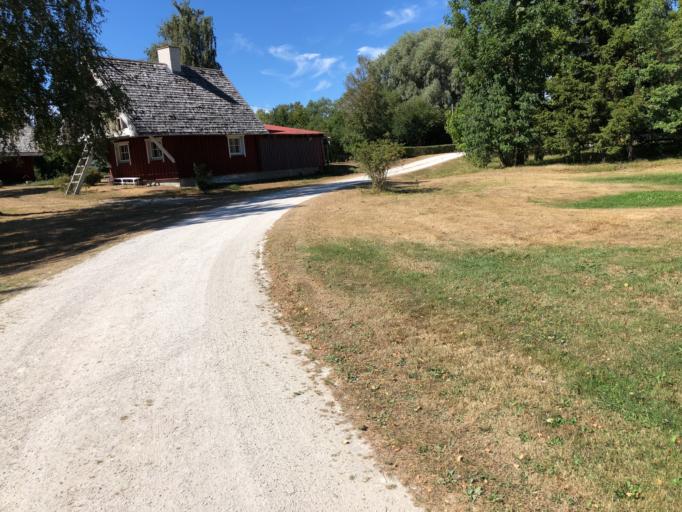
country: EE
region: Laeaene
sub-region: Haapsalu linn
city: Haapsalu
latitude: 58.7720
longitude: 23.5481
